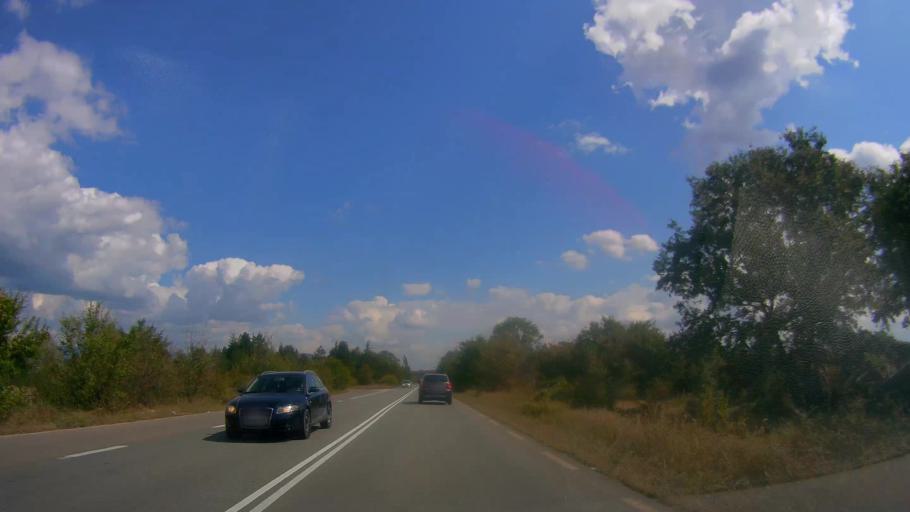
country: BG
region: Sliven
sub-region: Obshtina Tvurditsa
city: Tvurditsa
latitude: 42.6524
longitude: 25.9697
